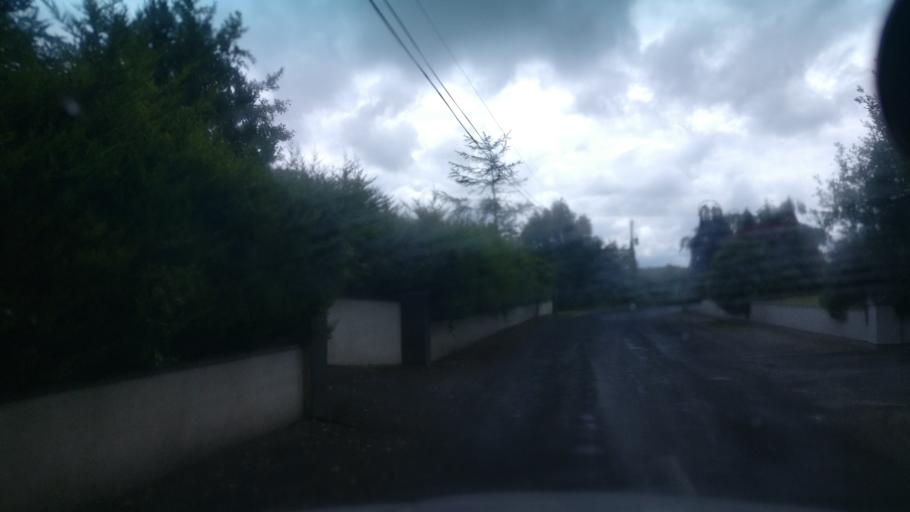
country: IE
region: Connaught
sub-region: County Galway
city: Loughrea
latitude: 53.1747
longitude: -8.5660
